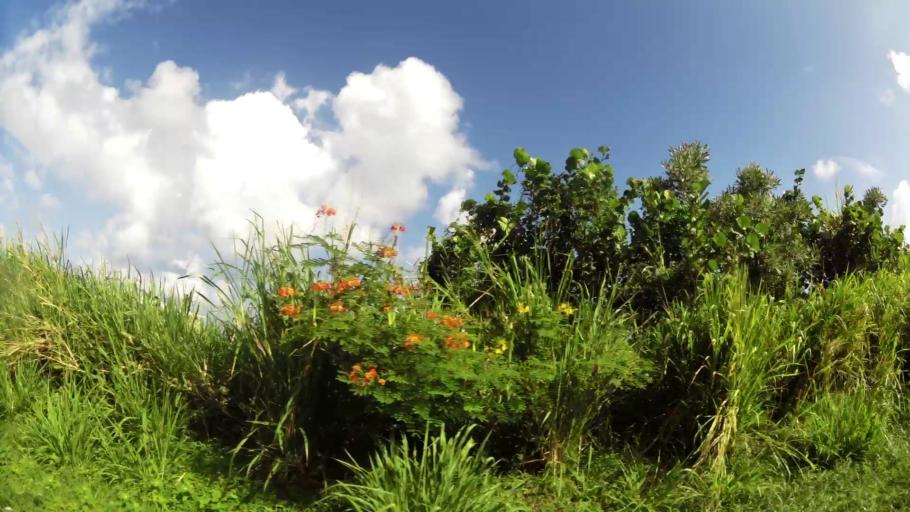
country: MQ
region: Martinique
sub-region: Martinique
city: Le Lorrain
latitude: 14.8328
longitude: -61.0421
